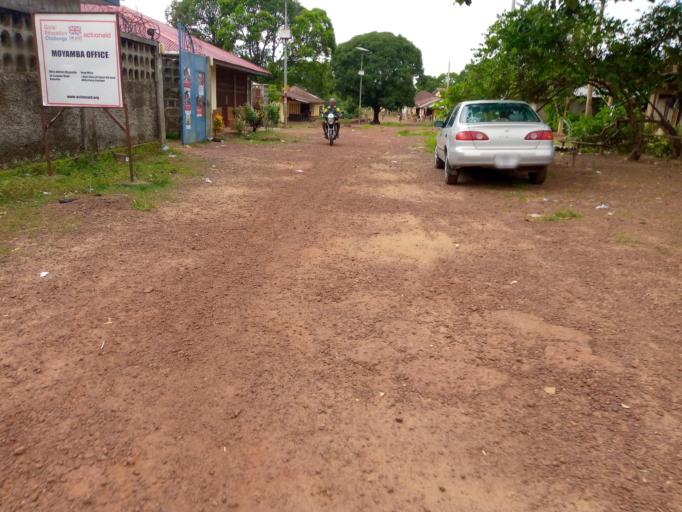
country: SL
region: Southern Province
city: Moyamba
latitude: 8.1527
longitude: -12.4339
